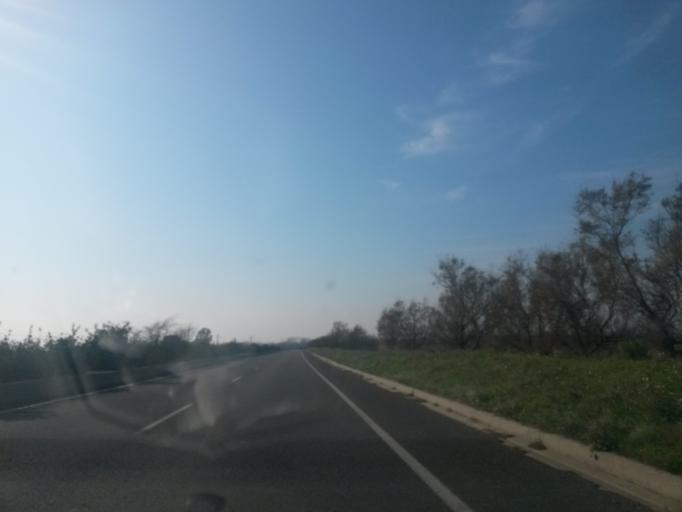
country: ES
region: Catalonia
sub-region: Provincia de Girona
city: Empuriabrava
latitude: 42.2697
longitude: 3.1301
